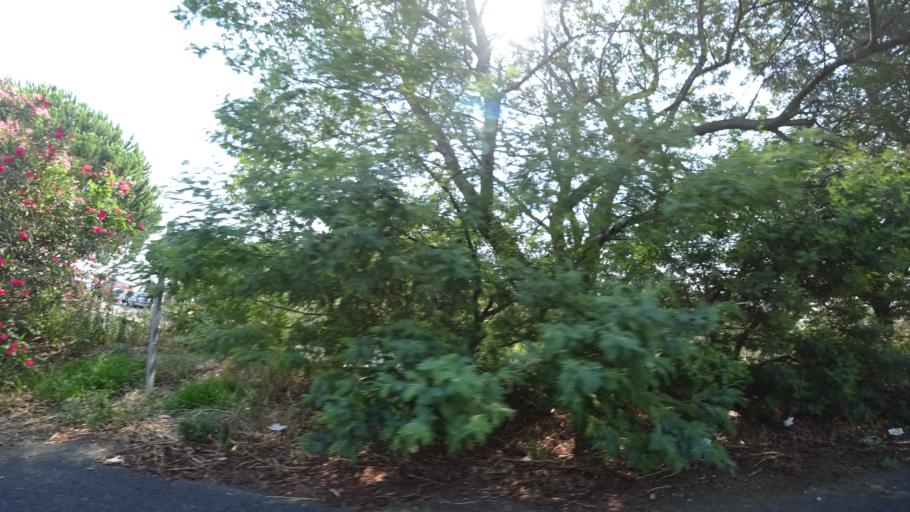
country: FR
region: Languedoc-Roussillon
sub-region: Departement des Pyrenees-Orientales
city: Bompas
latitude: 42.7156
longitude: 2.9322
